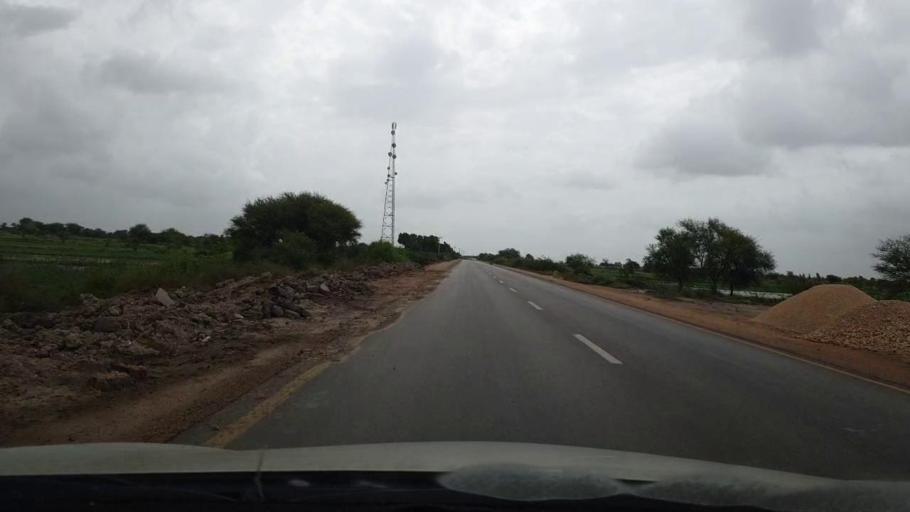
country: PK
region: Sindh
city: Mirpur Batoro
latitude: 24.6205
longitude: 68.3086
